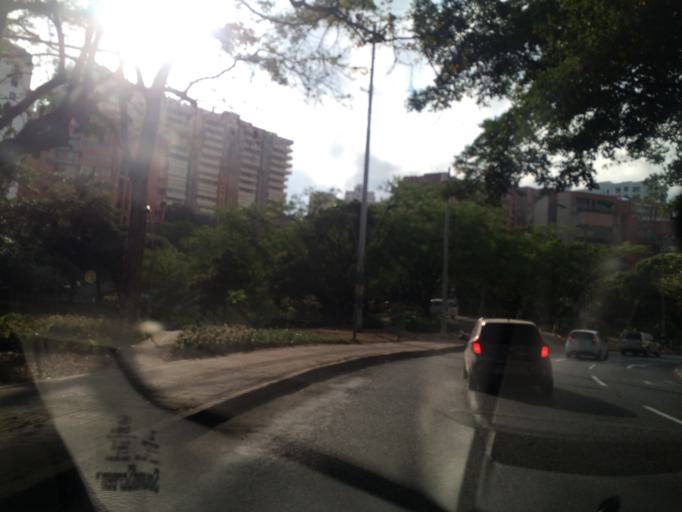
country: CO
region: Valle del Cauca
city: Cali
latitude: 3.4541
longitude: -76.5474
